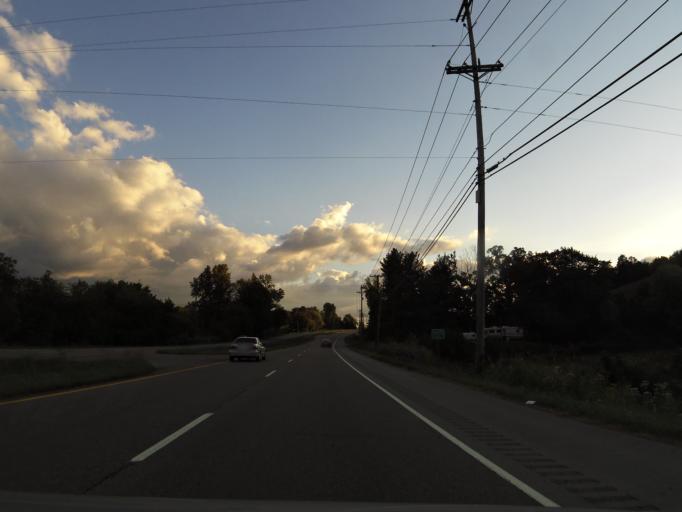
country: US
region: Tennessee
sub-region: Knox County
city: Mascot
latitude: 36.0469
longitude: -83.7113
